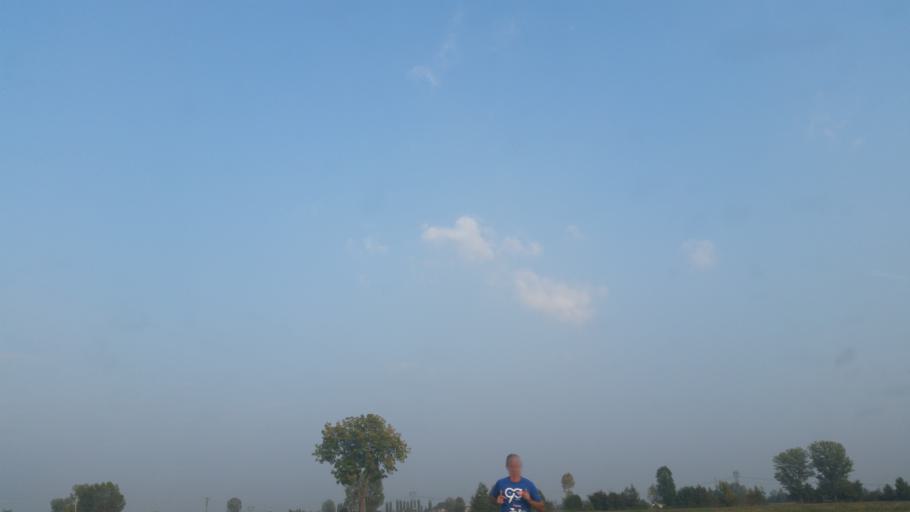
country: IT
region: Lombardy
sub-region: Provincia di Brescia
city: Azzano Mella
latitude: 45.4254
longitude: 10.1352
